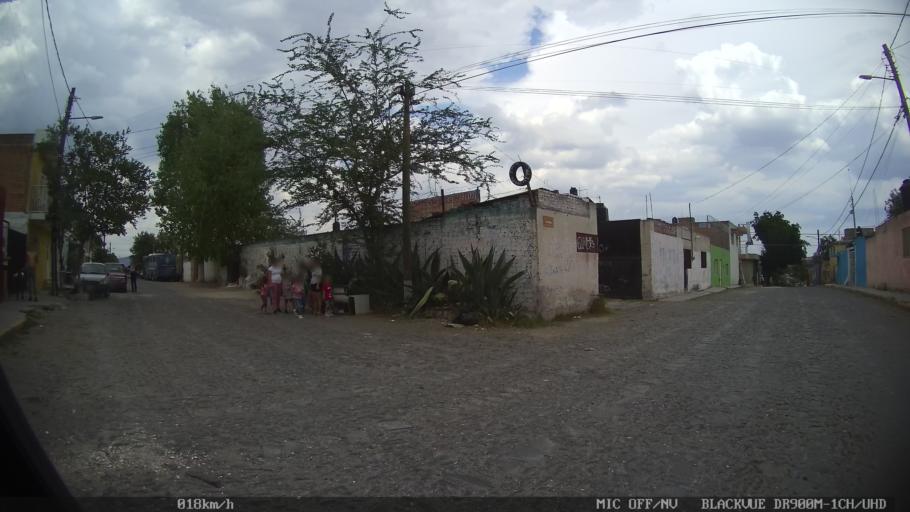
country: MX
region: Jalisco
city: Tlaquepaque
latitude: 20.6304
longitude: -103.2734
